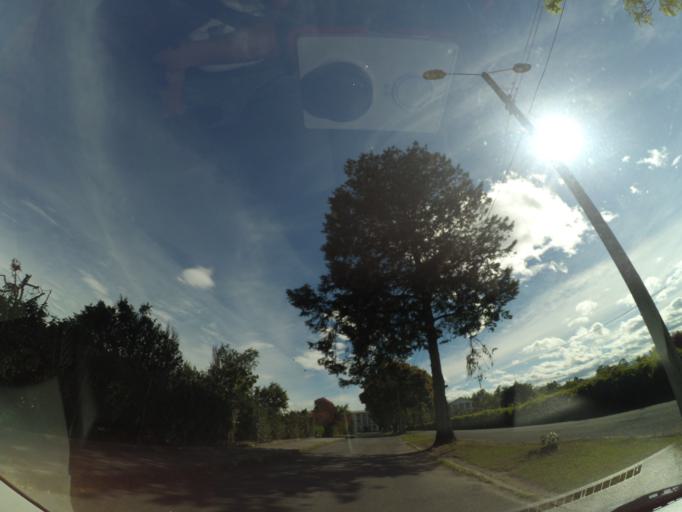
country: CO
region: Cauca
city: Popayan
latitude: 2.4616
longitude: -76.5923
